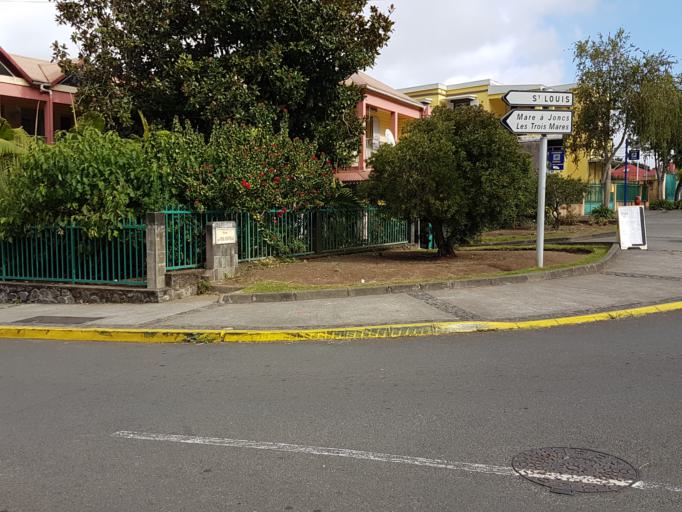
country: RE
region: Reunion
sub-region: Reunion
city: Cilaos
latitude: -21.1331
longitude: 55.4721
